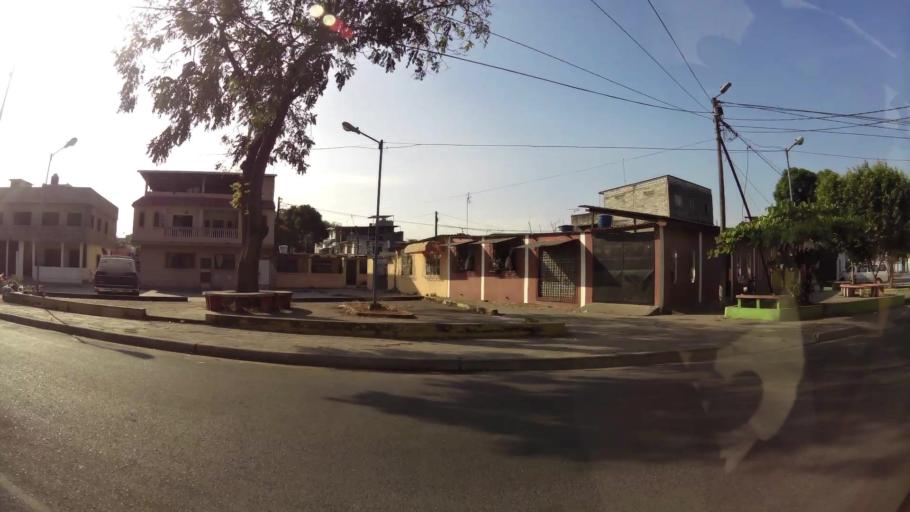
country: EC
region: Guayas
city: Eloy Alfaro
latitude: -2.1752
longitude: -79.8415
